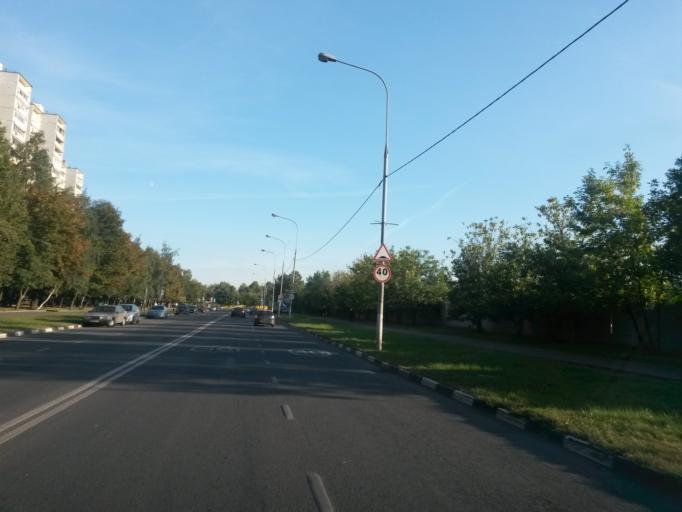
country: RU
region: Moscow
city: Orekhovo-Borisovo
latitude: 55.6048
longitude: 37.7254
